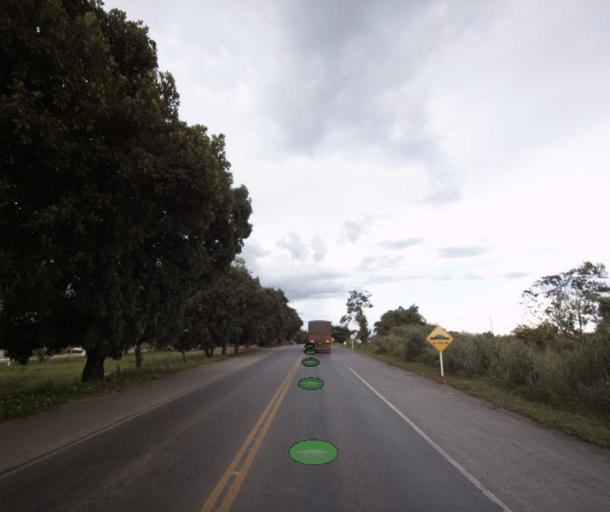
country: BR
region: Goias
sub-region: Itapaci
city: Itapaci
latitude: -15.0394
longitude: -49.4386
